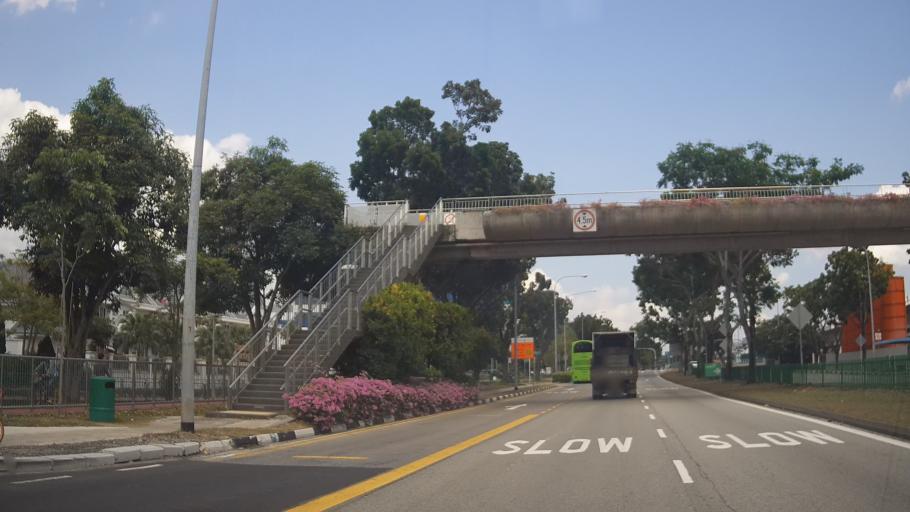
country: SG
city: Singapore
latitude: 1.3294
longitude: 103.9508
